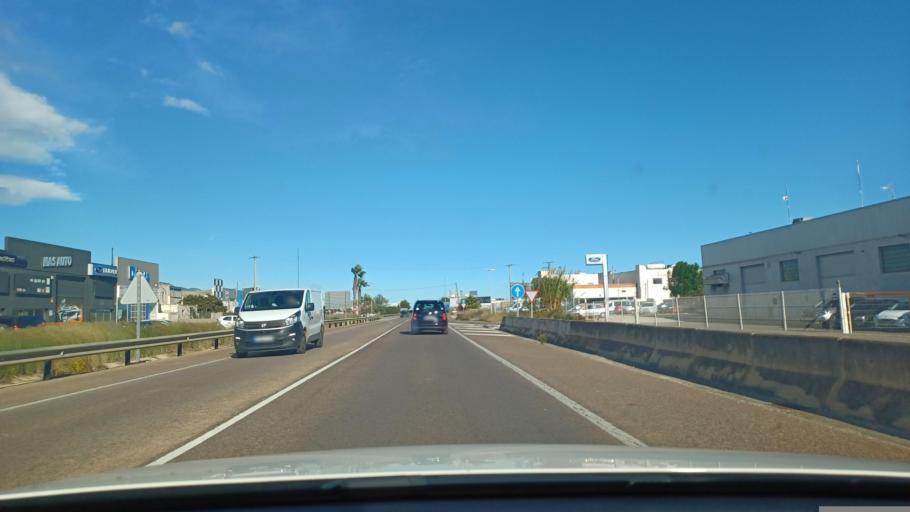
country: ES
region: Valencia
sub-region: Provincia de Castello
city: Vinaros
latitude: 40.4786
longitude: 0.4705
